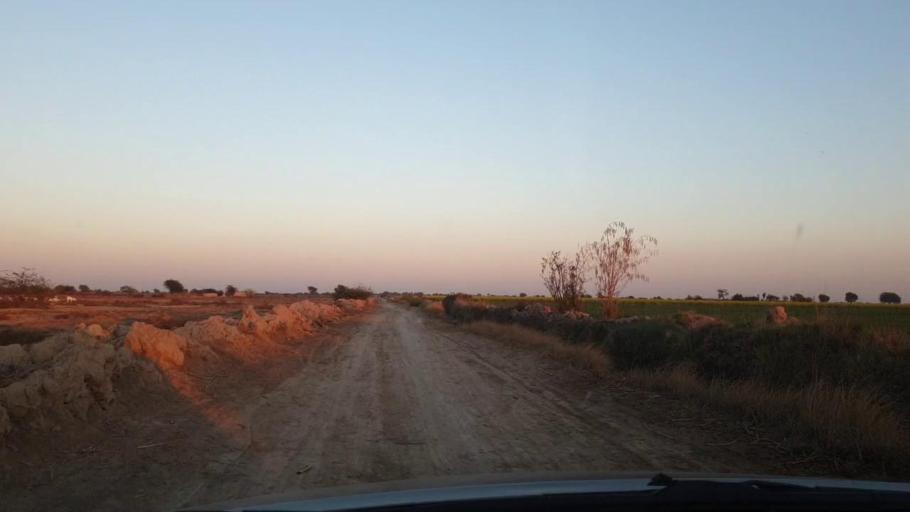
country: PK
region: Sindh
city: Tando Mittha Khan
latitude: 25.8565
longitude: 69.1947
